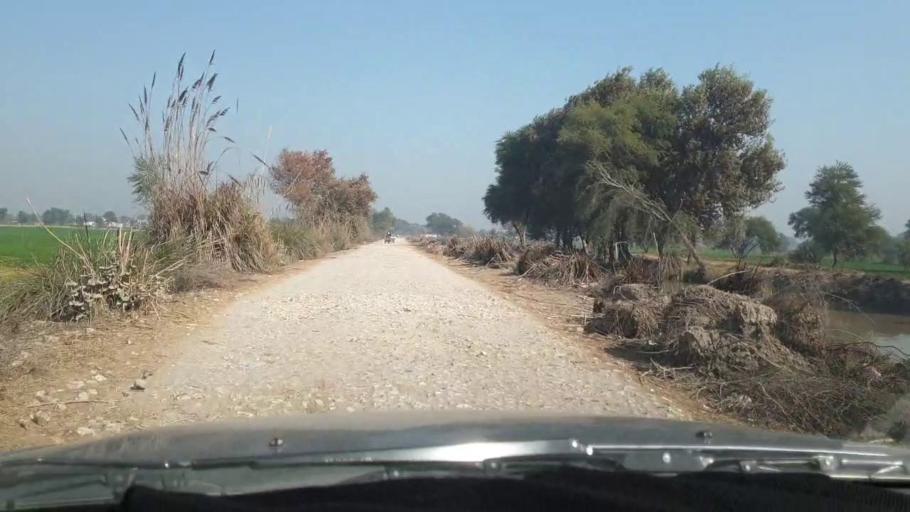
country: PK
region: Sindh
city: Khanpur
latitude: 27.8009
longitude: 69.5703
